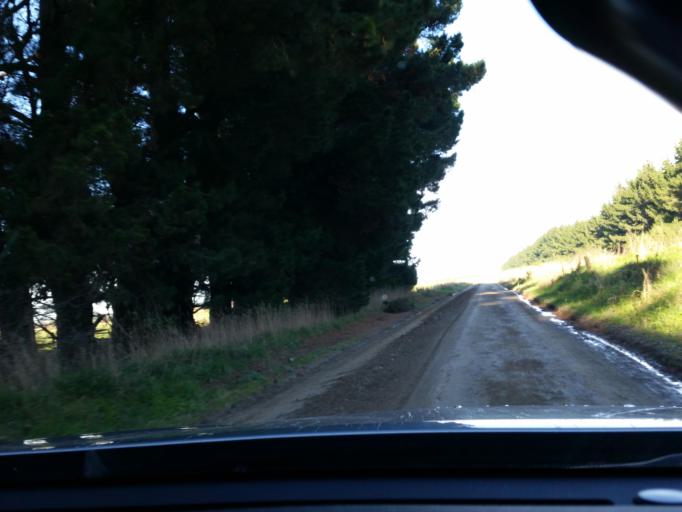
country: NZ
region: Southland
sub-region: Southland District
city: Winton
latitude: -46.2218
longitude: 168.4932
